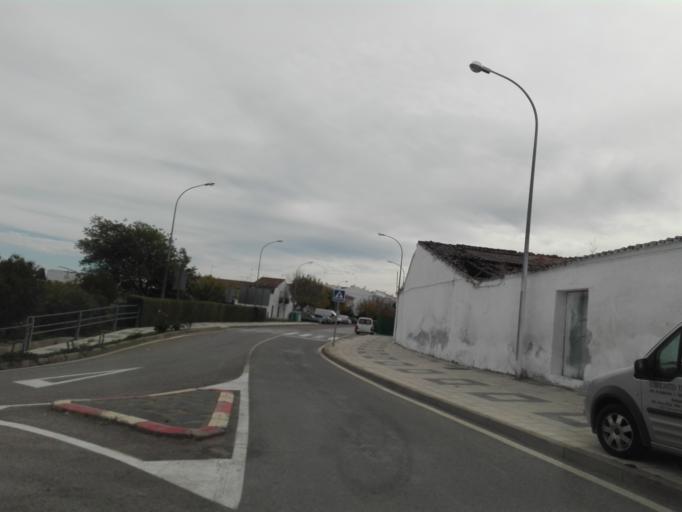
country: ES
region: Extremadura
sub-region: Provincia de Badajoz
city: Llerena
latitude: 38.2409
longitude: -6.0156
